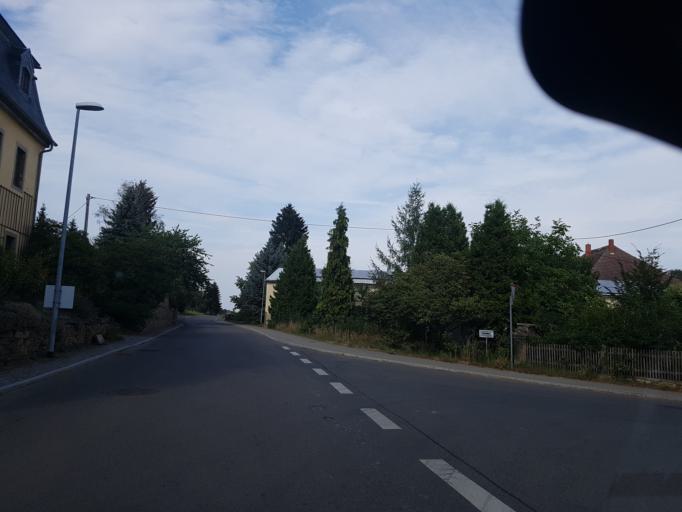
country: DE
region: Saxony
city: Ostrau
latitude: 51.2157
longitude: 13.1688
